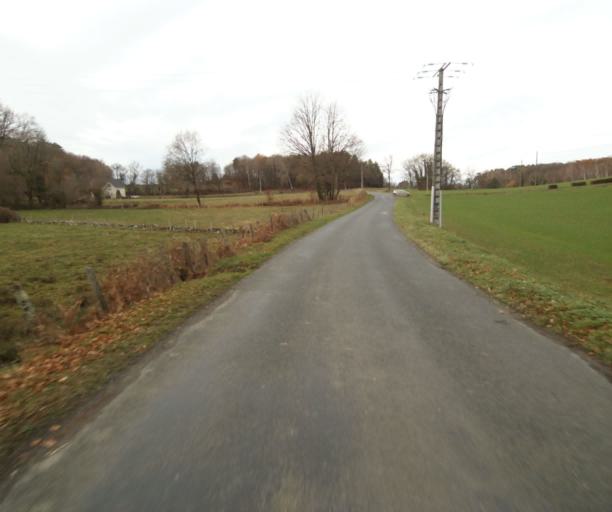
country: FR
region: Limousin
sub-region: Departement de la Correze
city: Chameyrat
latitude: 45.2501
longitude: 1.6825
